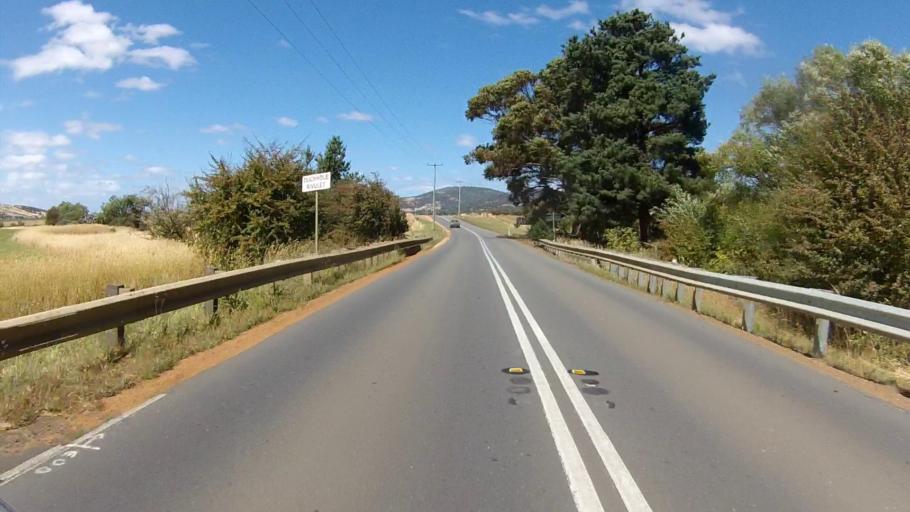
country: AU
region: Tasmania
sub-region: Clarence
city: Cambridge
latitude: -42.7547
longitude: 147.4165
